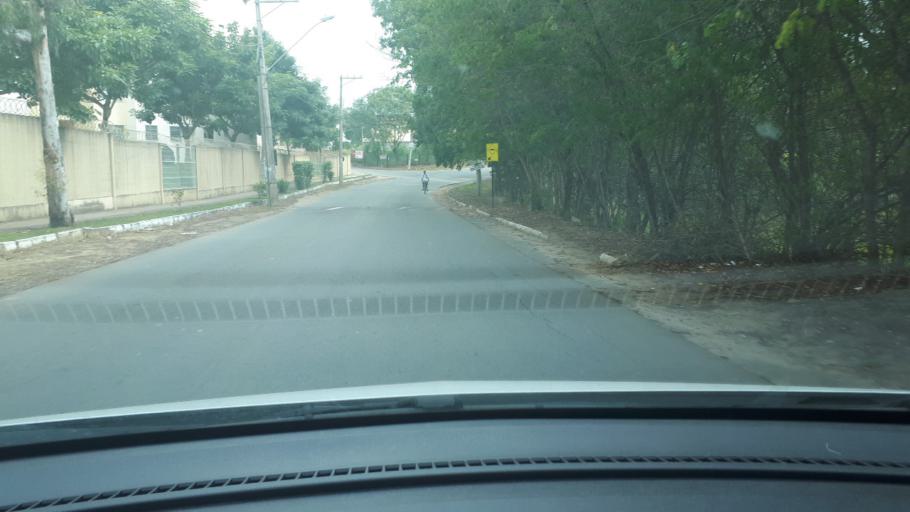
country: BR
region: Espirito Santo
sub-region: Serra
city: Serra
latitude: -20.1466
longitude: -40.1974
